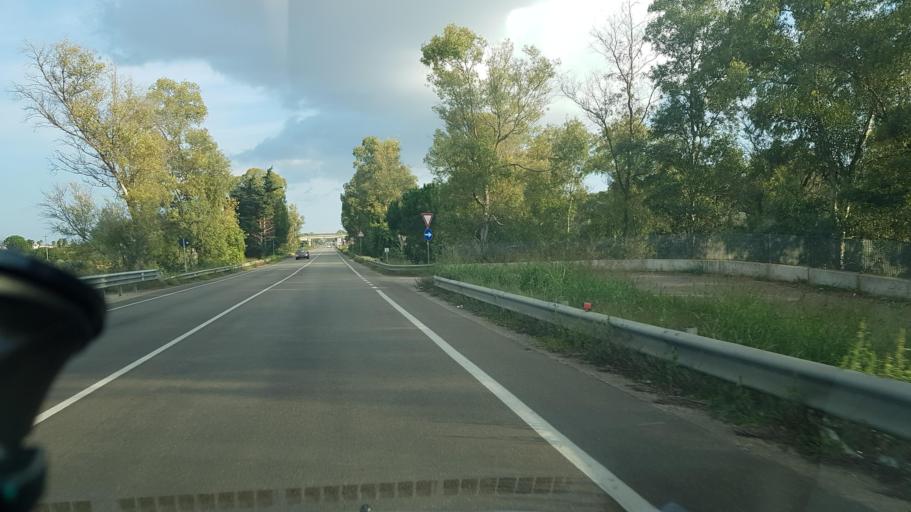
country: IT
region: Apulia
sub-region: Provincia di Lecce
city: Acquarica del Capo
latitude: 39.9035
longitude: 18.2458
